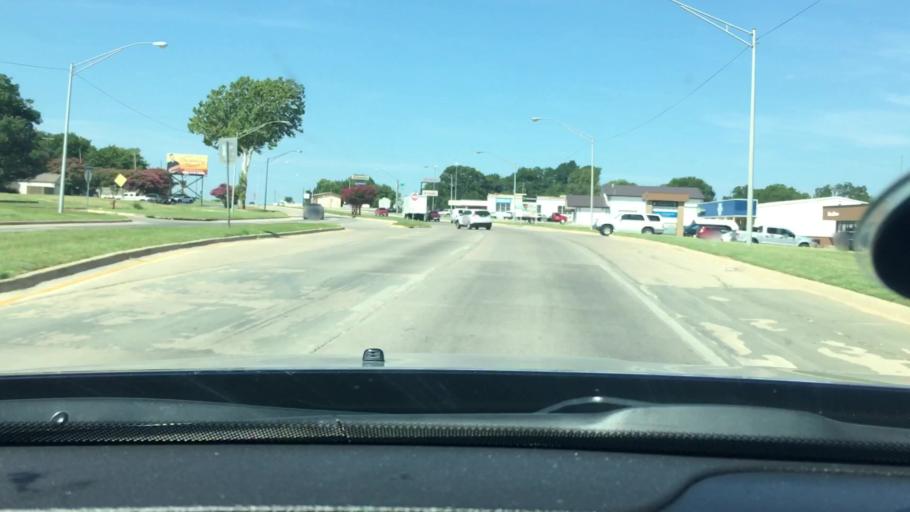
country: US
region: Oklahoma
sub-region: Carter County
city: Ardmore
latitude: 34.1745
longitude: -97.1464
